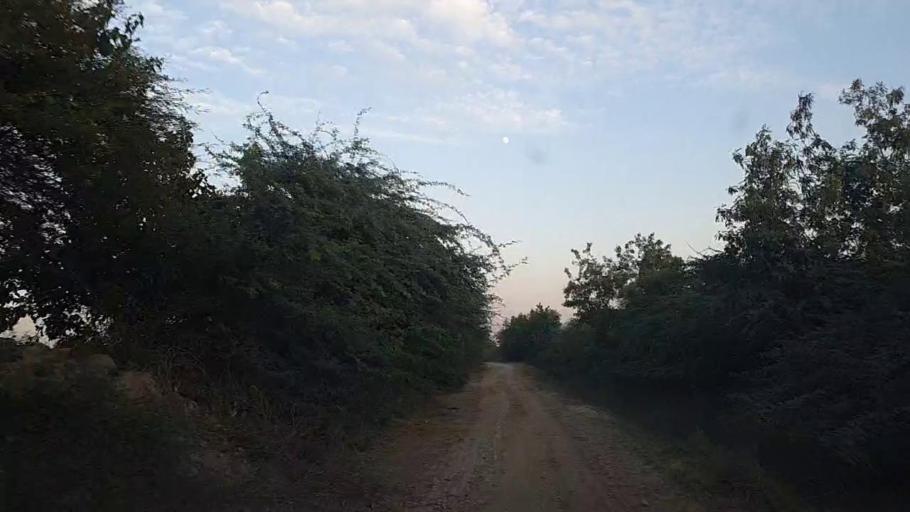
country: PK
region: Sindh
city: Thatta
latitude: 24.7915
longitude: 67.9199
